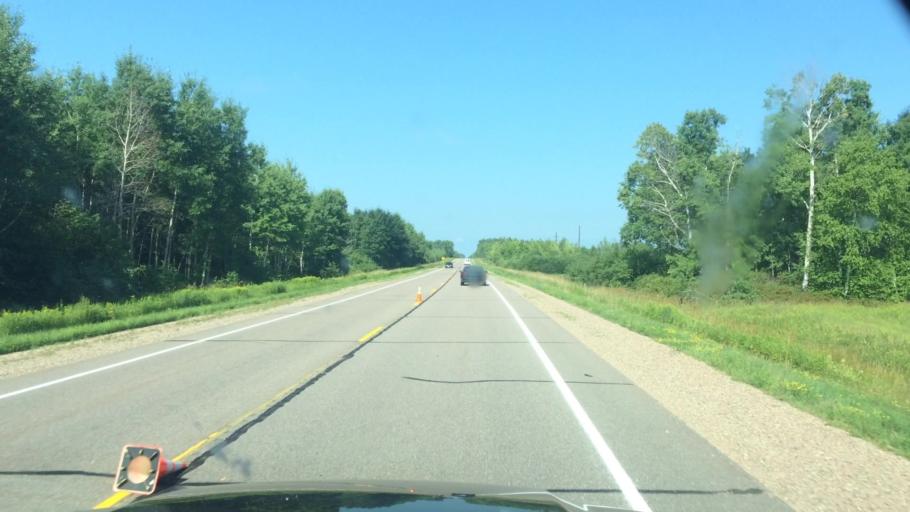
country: US
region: Wisconsin
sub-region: Langlade County
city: Antigo
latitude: 45.1468
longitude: -89.3441
